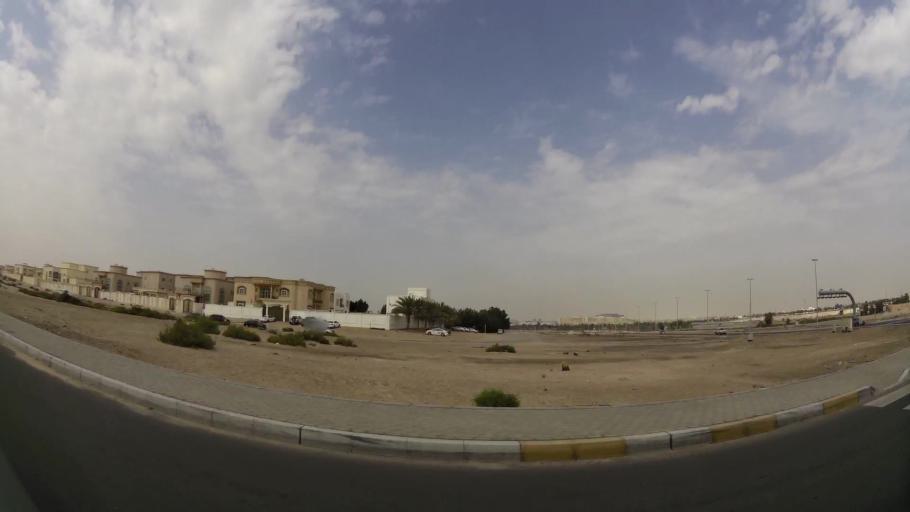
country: AE
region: Abu Dhabi
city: Abu Dhabi
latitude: 24.3007
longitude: 54.6337
